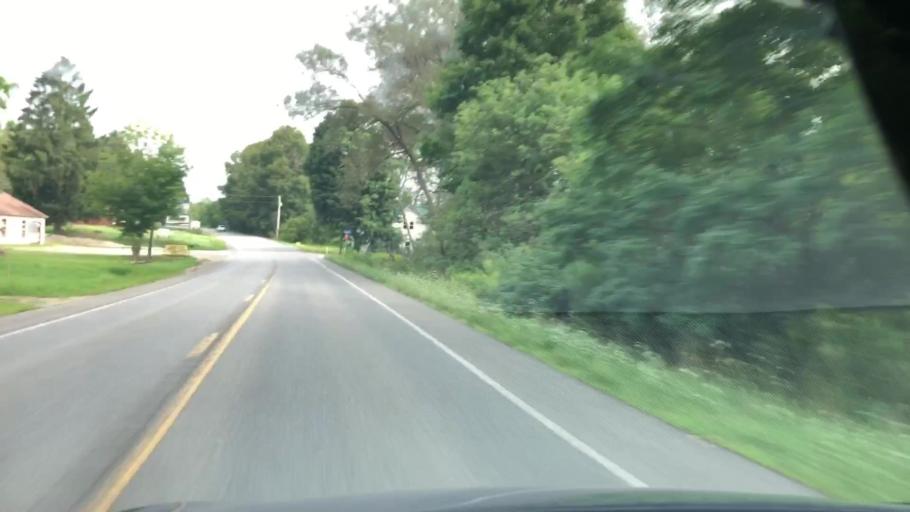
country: US
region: Pennsylvania
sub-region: Erie County
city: Union City
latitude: 41.8348
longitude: -79.8185
